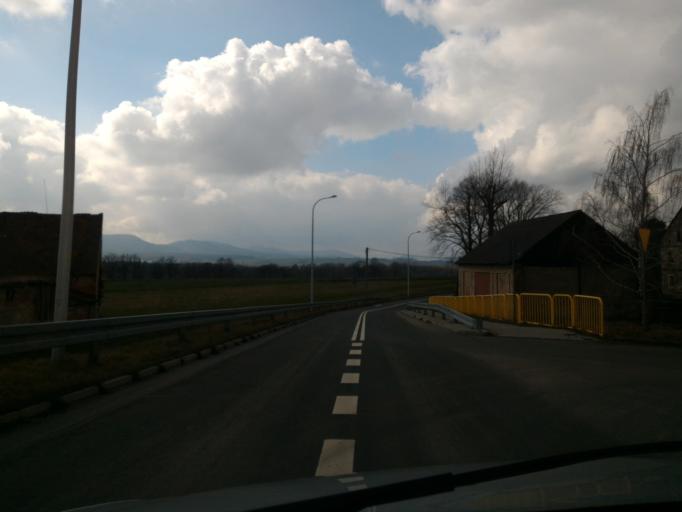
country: CZ
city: Hradek nad Nisou
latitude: 50.8714
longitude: 14.8449
